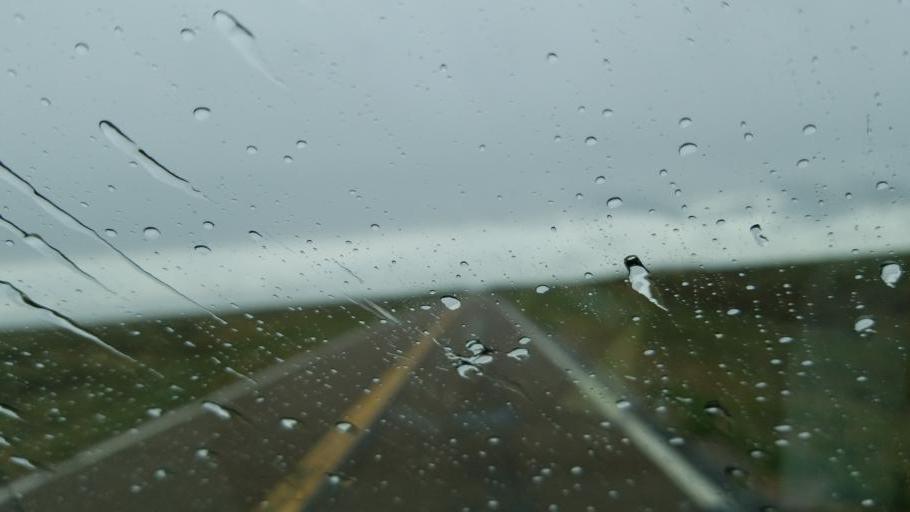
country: US
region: Colorado
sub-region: Lincoln County
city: Hugo
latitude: 38.8494
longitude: -103.2421
